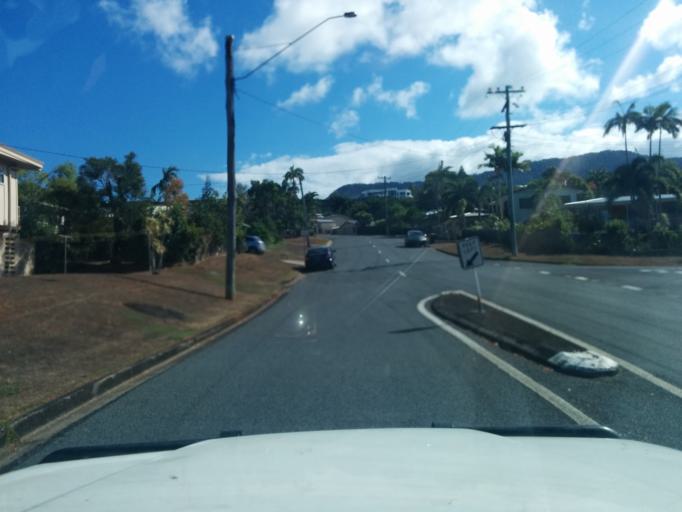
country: AU
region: Queensland
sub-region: Cairns
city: Woree
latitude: -16.9492
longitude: 145.7333
